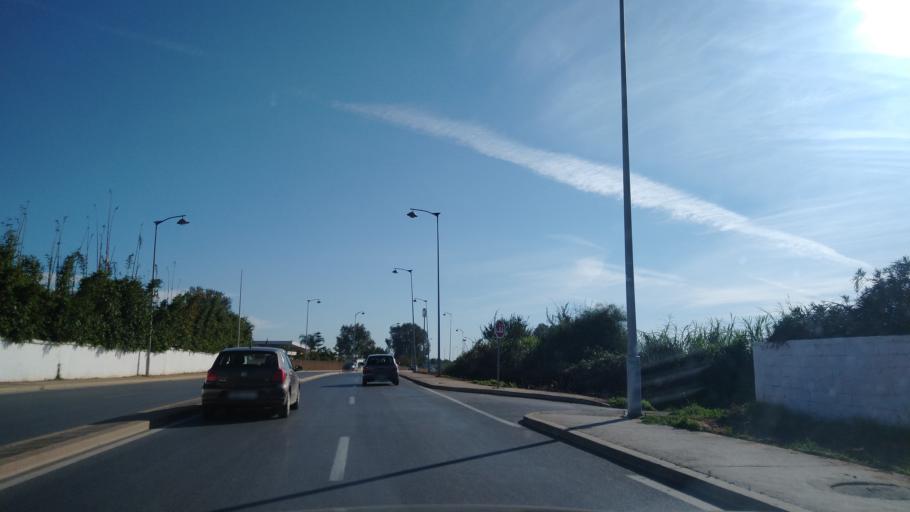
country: MA
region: Rabat-Sale-Zemmour-Zaer
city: Sale
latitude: 34.0231
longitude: -6.7350
